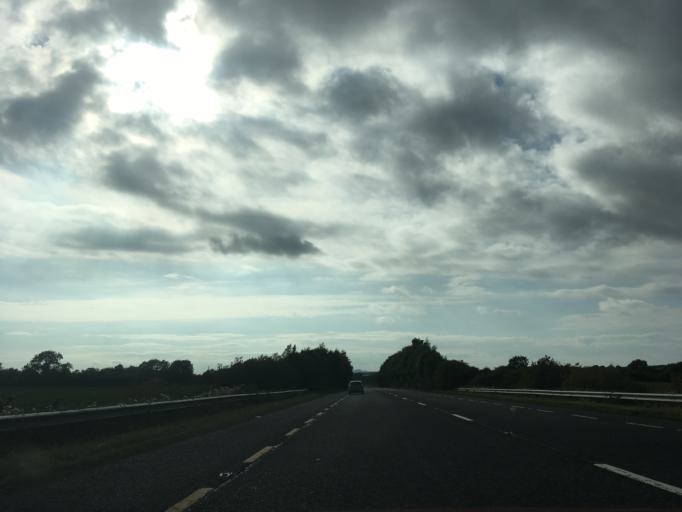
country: IE
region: Leinster
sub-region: Loch Garman
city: Loch Garman
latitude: 52.3455
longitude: -6.5969
